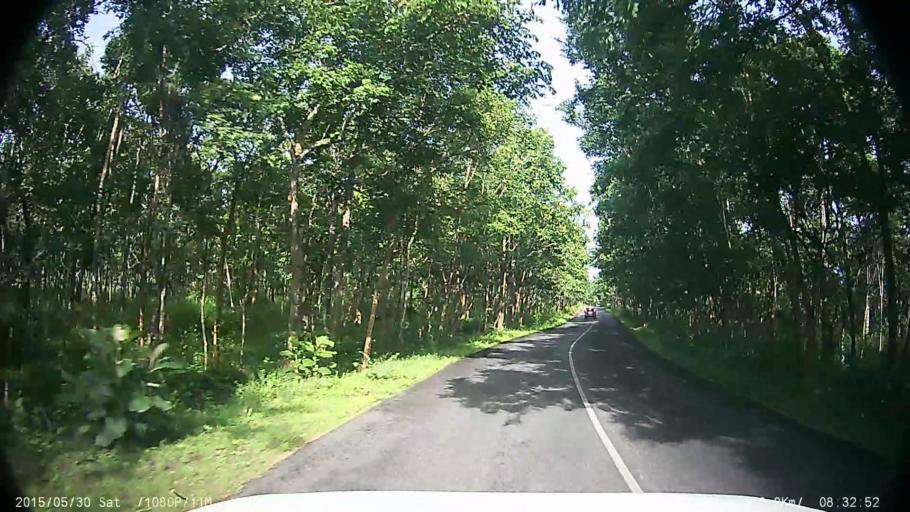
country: IN
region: Tamil Nadu
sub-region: Nilgiri
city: Masinigudi
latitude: 11.7287
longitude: 76.4517
